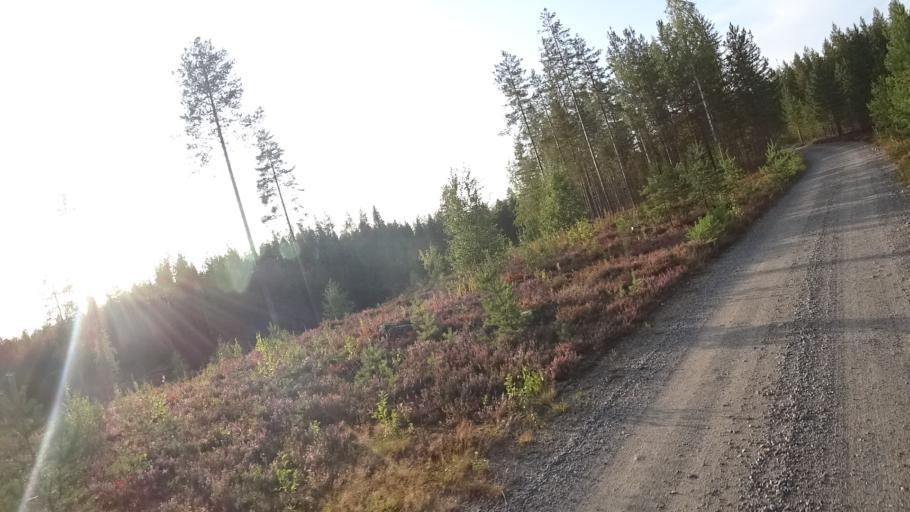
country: FI
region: North Karelia
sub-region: Joensuu
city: Ilomantsi
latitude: 62.6346
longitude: 31.0810
